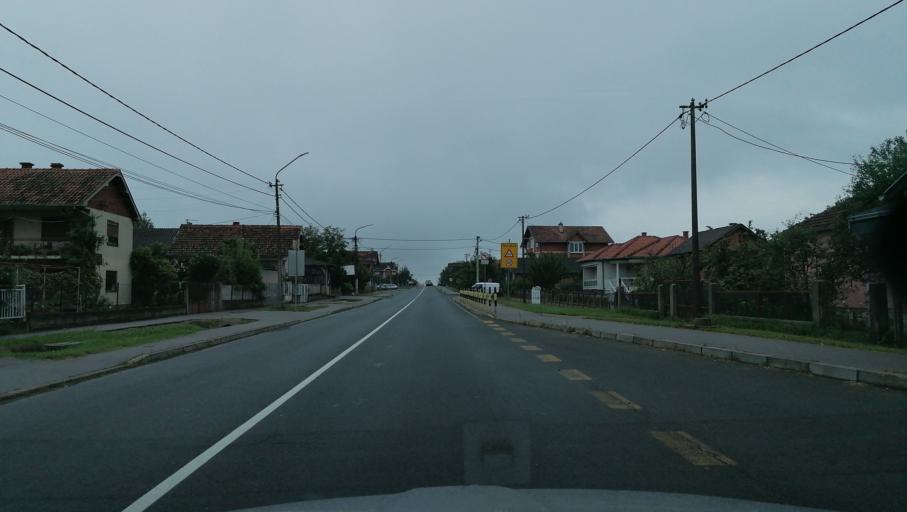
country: RS
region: Central Serbia
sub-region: Rasinski Okrug
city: Krusevac
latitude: 43.5877
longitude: 21.2705
